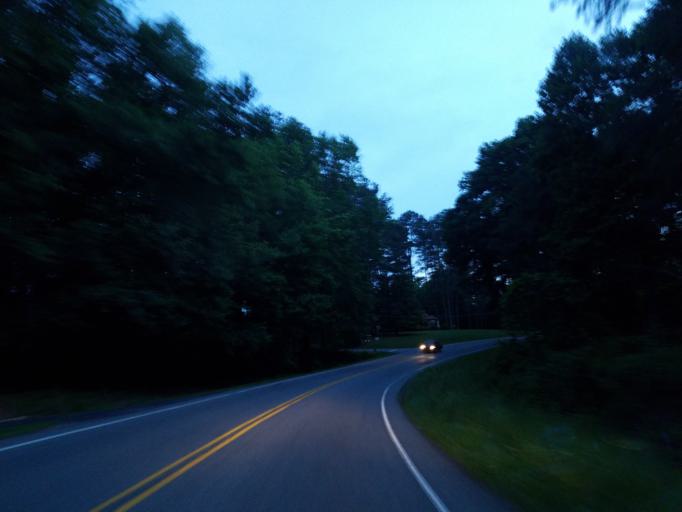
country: US
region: Georgia
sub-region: Dawson County
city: Dawsonville
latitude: 34.4035
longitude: -84.1195
